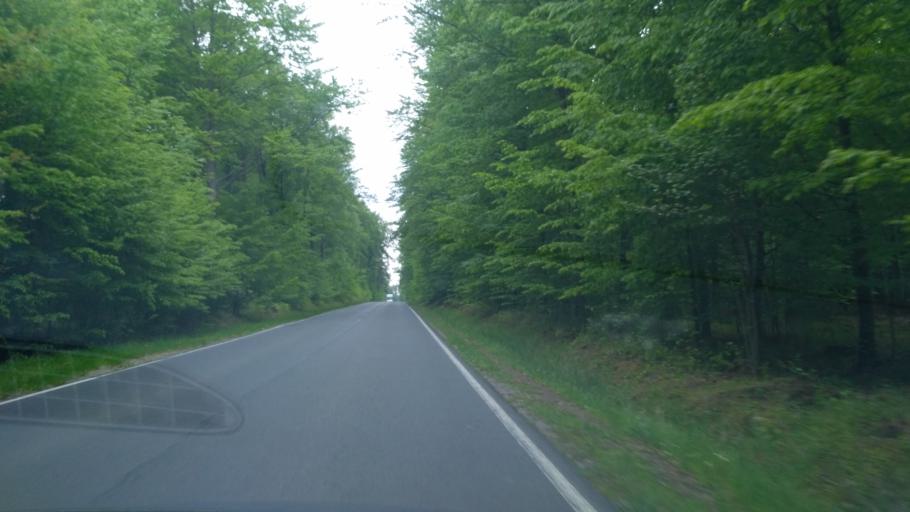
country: PL
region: Subcarpathian Voivodeship
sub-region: Powiat kolbuszowski
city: Kolbuszowa
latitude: 50.1613
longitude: 21.7592
